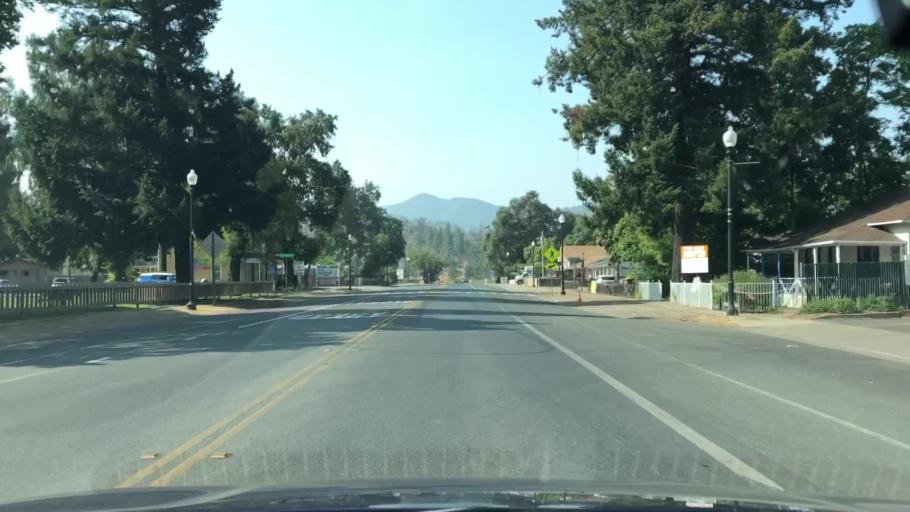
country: US
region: California
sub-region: Lake County
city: Middletown
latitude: 38.7506
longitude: -122.6160
